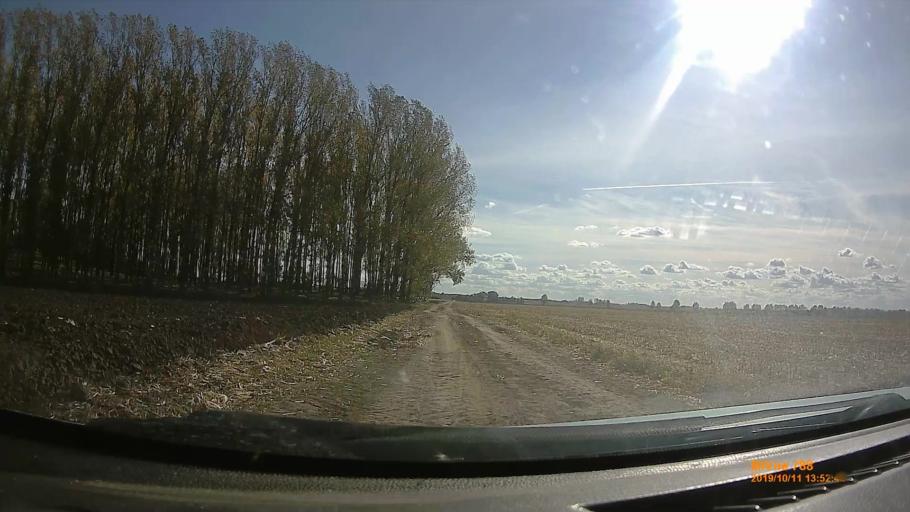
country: HU
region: Hajdu-Bihar
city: Hajduszoboszlo
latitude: 47.5394
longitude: 21.4010
